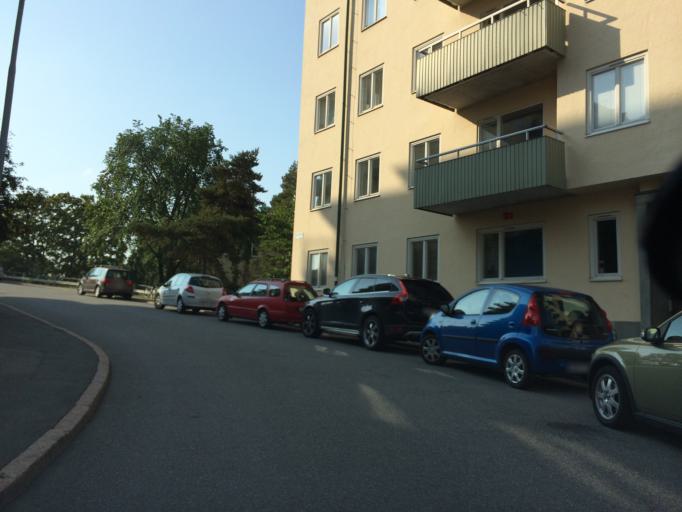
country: SE
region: Stockholm
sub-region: Solna Kommun
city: Solna
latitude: 59.3306
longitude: 17.9986
